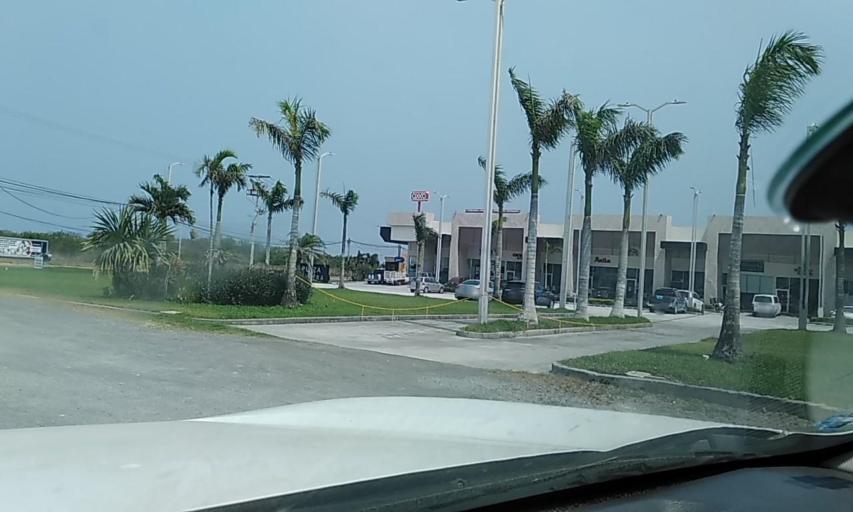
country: MX
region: Veracruz
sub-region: Alvarado
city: Playa de la Libertad
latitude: 19.0719
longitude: -96.0870
